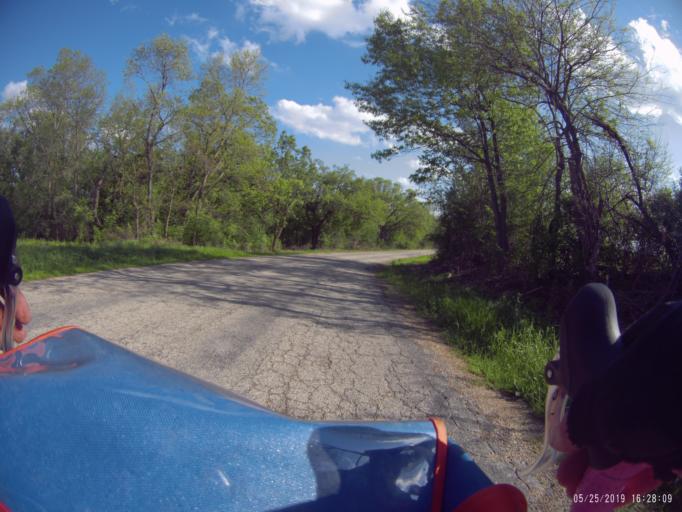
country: US
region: Wisconsin
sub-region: Dane County
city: Mount Horeb
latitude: 42.9485
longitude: -89.7065
